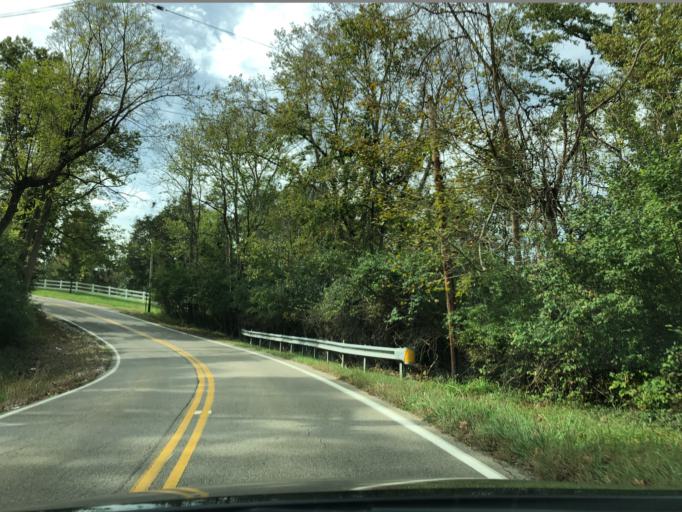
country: US
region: Ohio
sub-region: Hamilton County
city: The Village of Indian Hill
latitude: 39.2330
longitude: -84.2987
